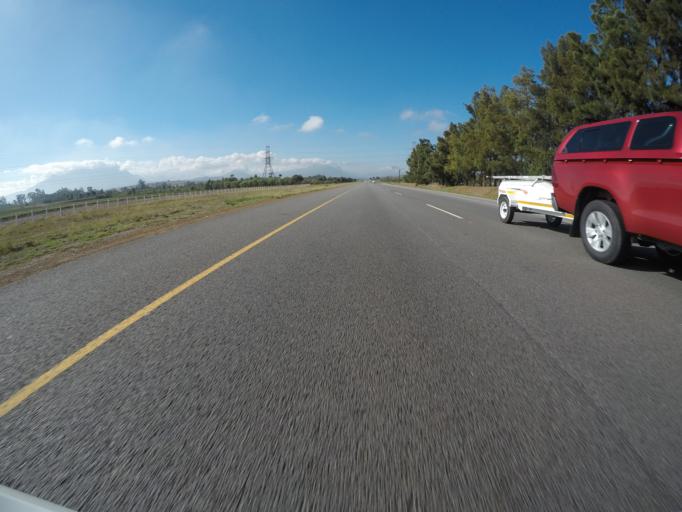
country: ZA
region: Western Cape
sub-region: City of Cape Town
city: Kraaifontein
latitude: -33.8490
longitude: 18.8046
